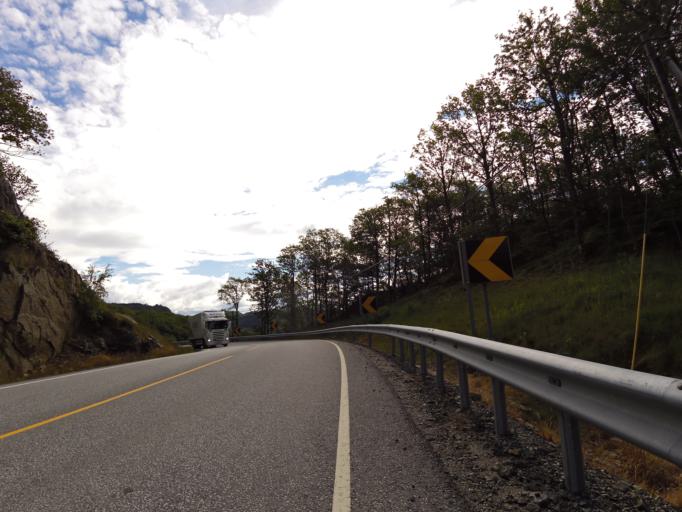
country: NO
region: Vest-Agder
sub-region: Lyngdal
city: Lyngdal
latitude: 58.0491
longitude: 7.1730
